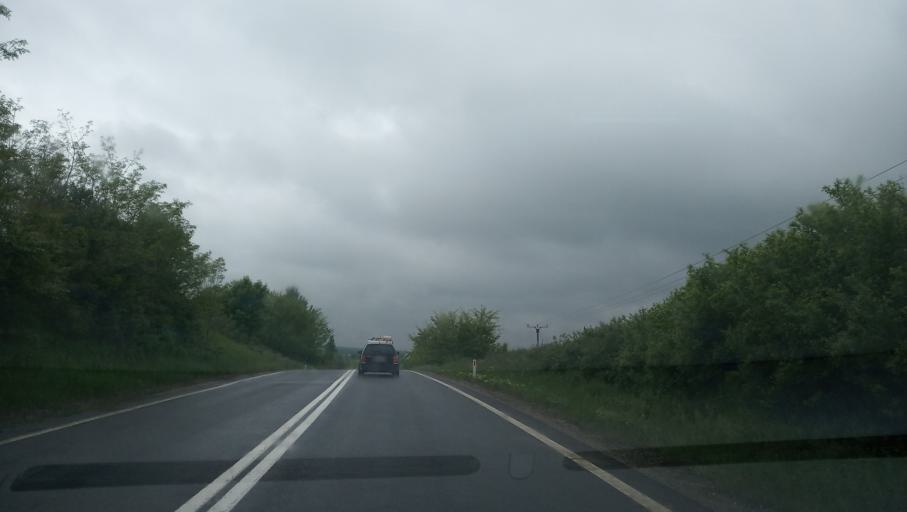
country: RO
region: Alba
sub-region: Comuna Cut
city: Cut
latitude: 45.9206
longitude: 23.6335
